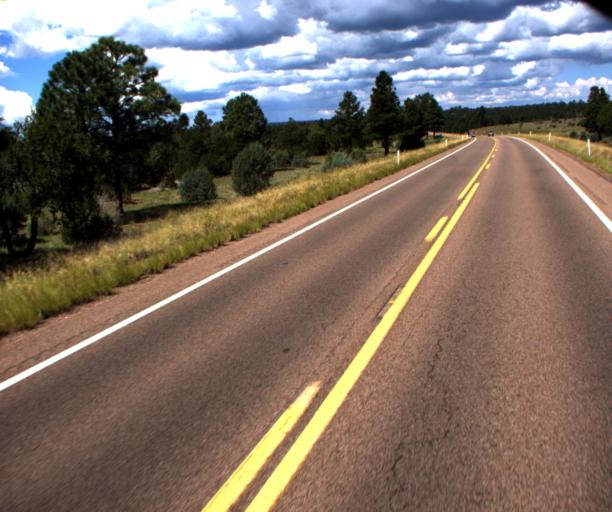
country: US
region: Arizona
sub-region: Navajo County
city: Heber-Overgaard
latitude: 34.3918
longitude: -110.5097
